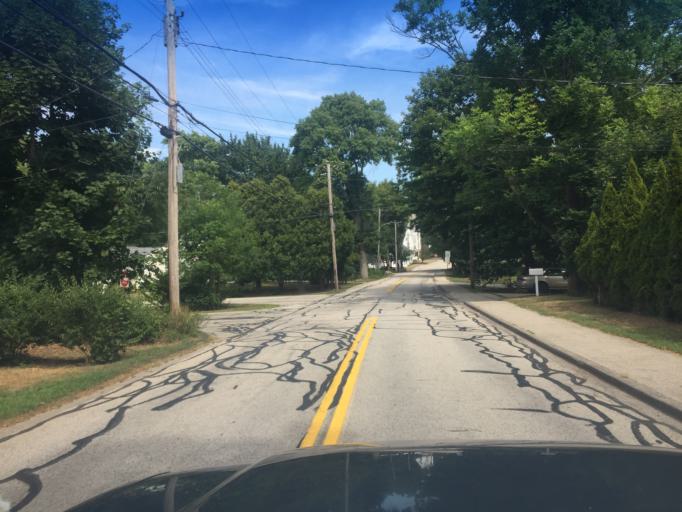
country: US
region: Maine
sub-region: York County
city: York Harbor
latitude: 43.1466
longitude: -70.6628
